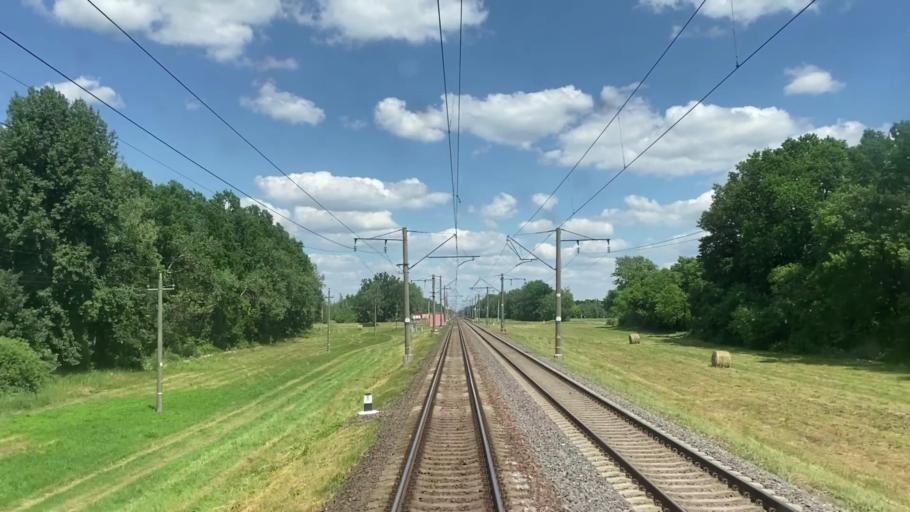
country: BY
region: Brest
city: Zhabinka
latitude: 52.2318
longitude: 24.0828
